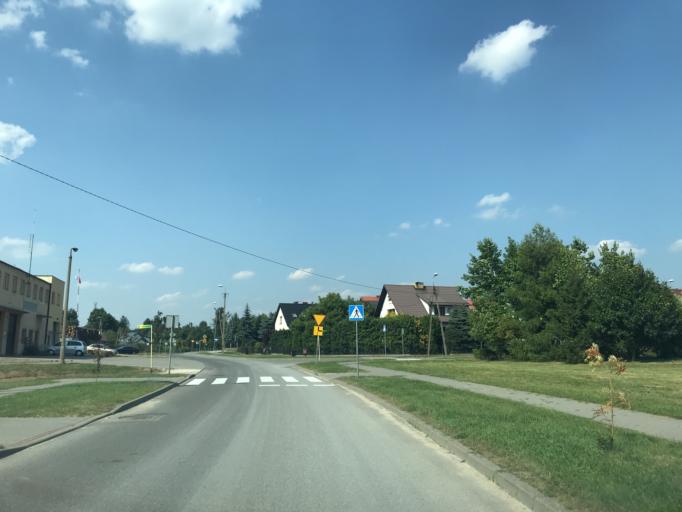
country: PL
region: Kujawsko-Pomorskie
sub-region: Powiat brodnicki
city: Gorzno
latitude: 53.1954
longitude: 19.6397
